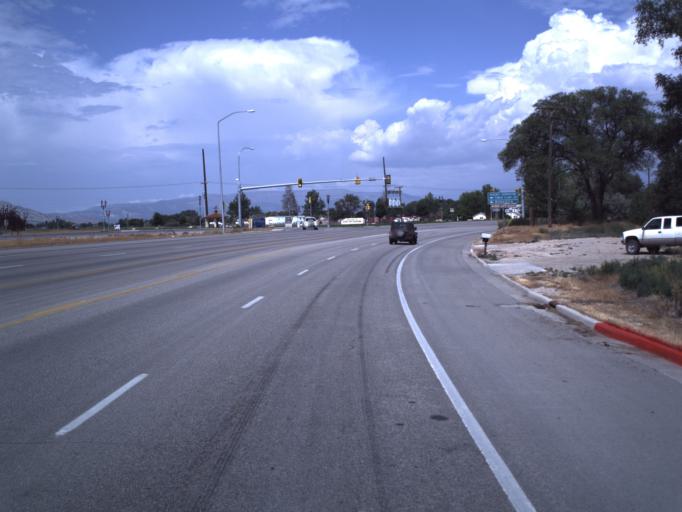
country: US
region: Utah
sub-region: Uintah County
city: Naples
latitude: 40.4137
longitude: -109.4972
